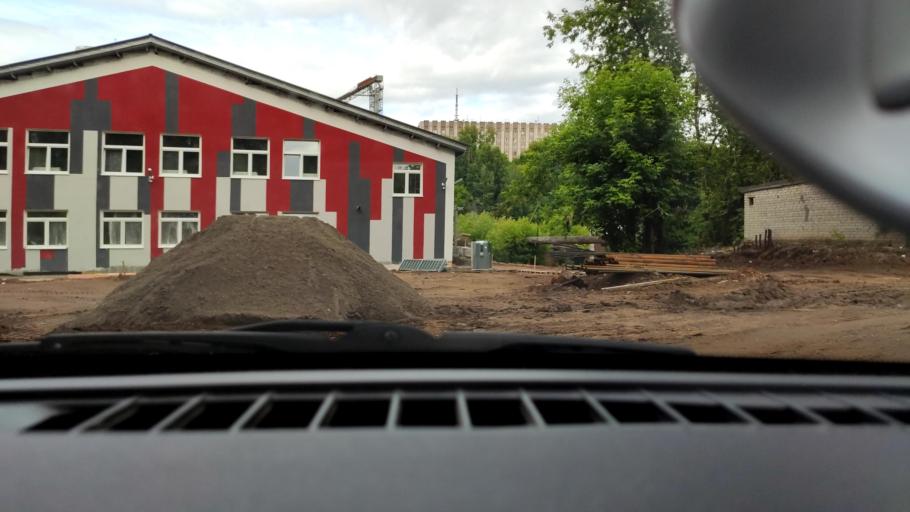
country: RU
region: Perm
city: Perm
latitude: 58.0100
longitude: 56.2740
